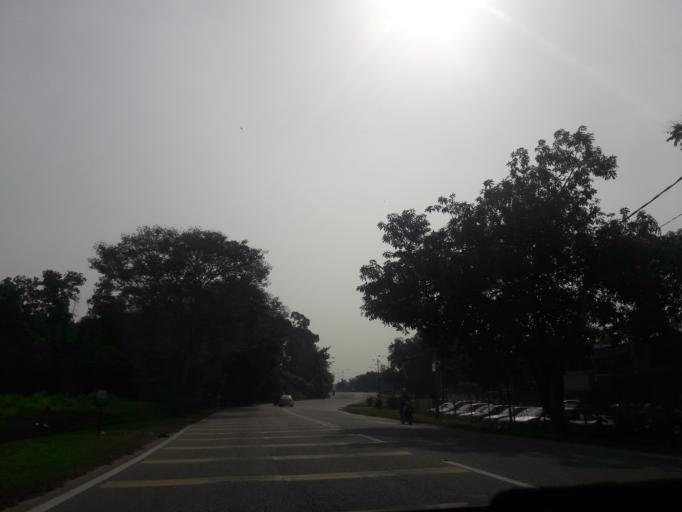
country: MY
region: Kedah
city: Kulim
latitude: 5.3494
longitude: 100.5251
